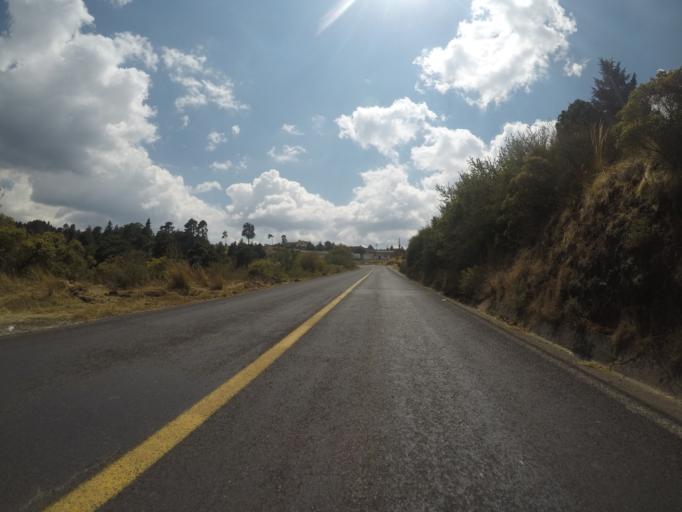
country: MX
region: Mexico
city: Cerro La Calera
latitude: 19.1722
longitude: -99.8054
